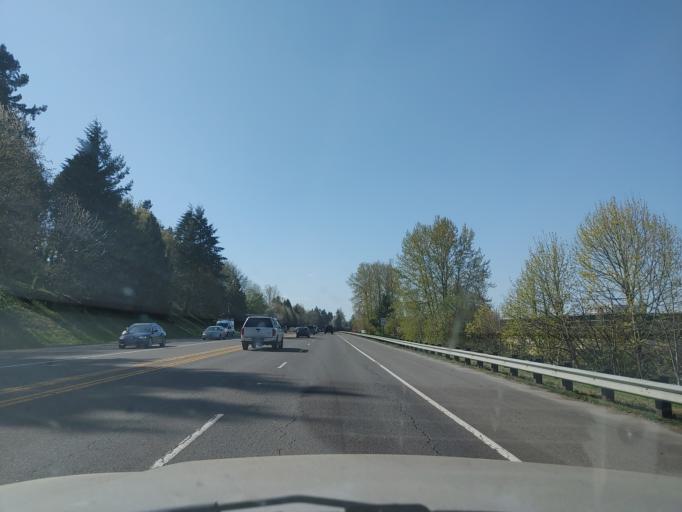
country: US
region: Oregon
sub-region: Clackamas County
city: Milwaukie
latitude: 45.4344
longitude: -122.6164
